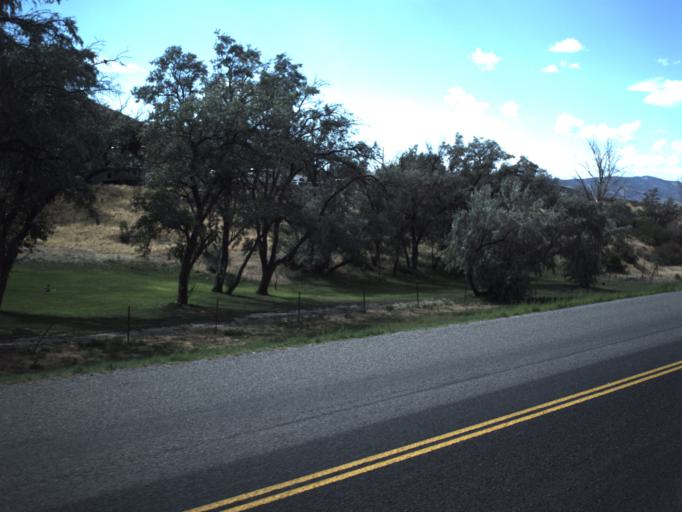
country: US
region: Utah
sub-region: Sevier County
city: Salina
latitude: 38.9446
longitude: -111.8554
